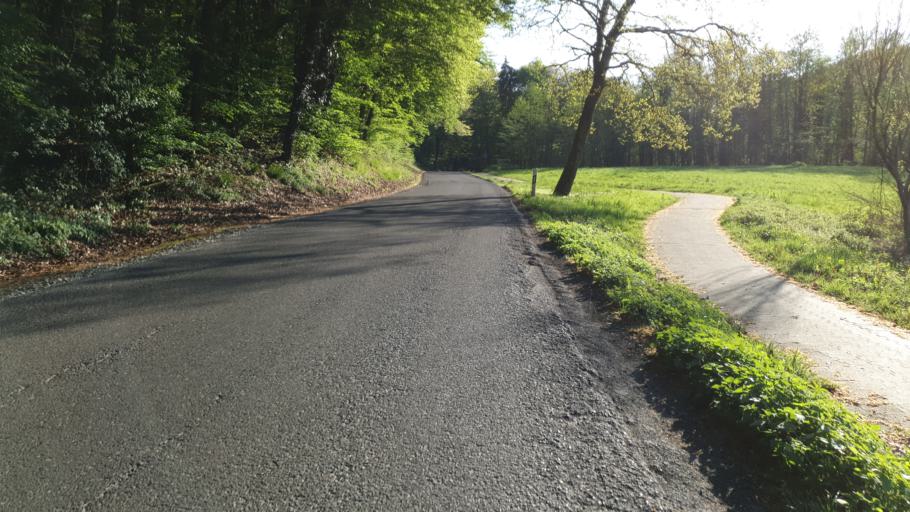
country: DE
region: North Rhine-Westphalia
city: Opladen
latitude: 51.0742
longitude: 7.0670
